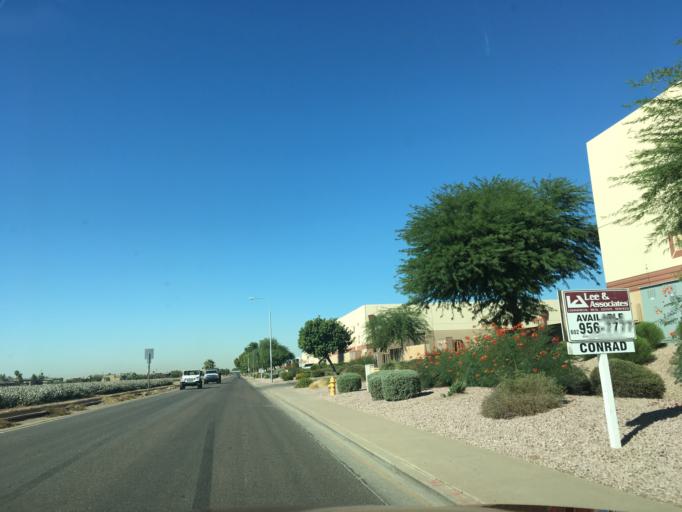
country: US
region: Arizona
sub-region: Maricopa County
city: Glendale
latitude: 33.4587
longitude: -112.1757
